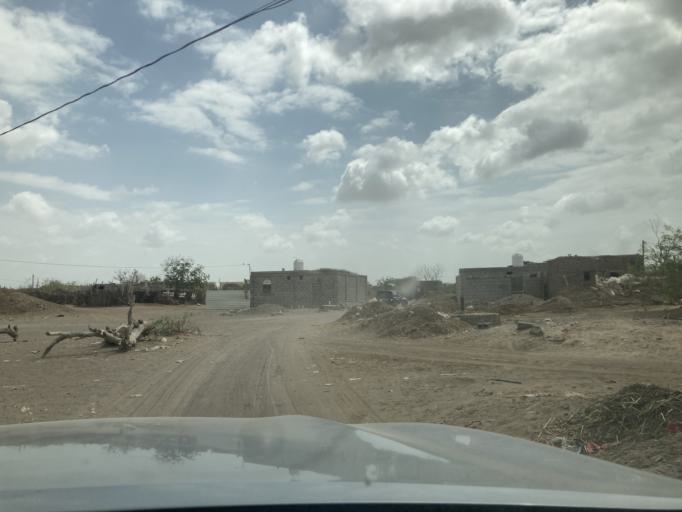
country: YE
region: Lahij
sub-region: Al  Hawtah
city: Lahij
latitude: 13.0200
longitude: 45.0024
